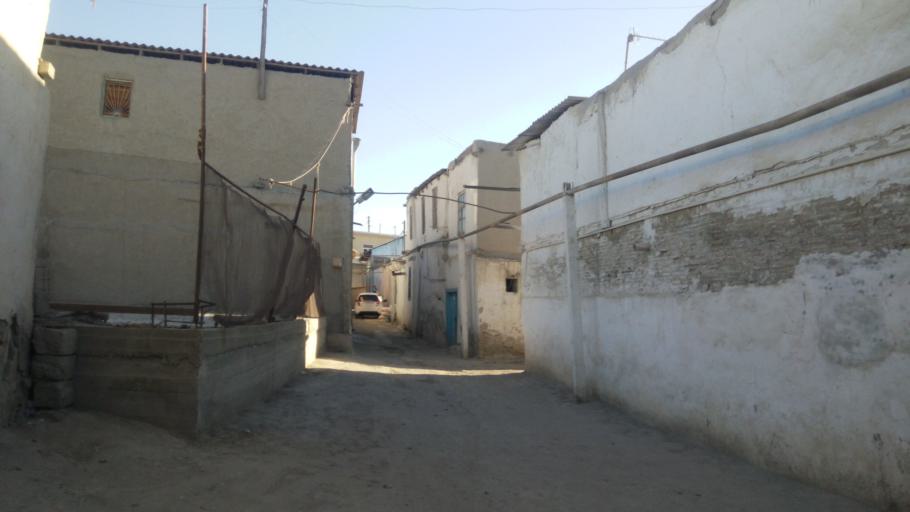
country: UZ
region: Bukhara
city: Bukhara
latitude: 39.7749
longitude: 64.4253
